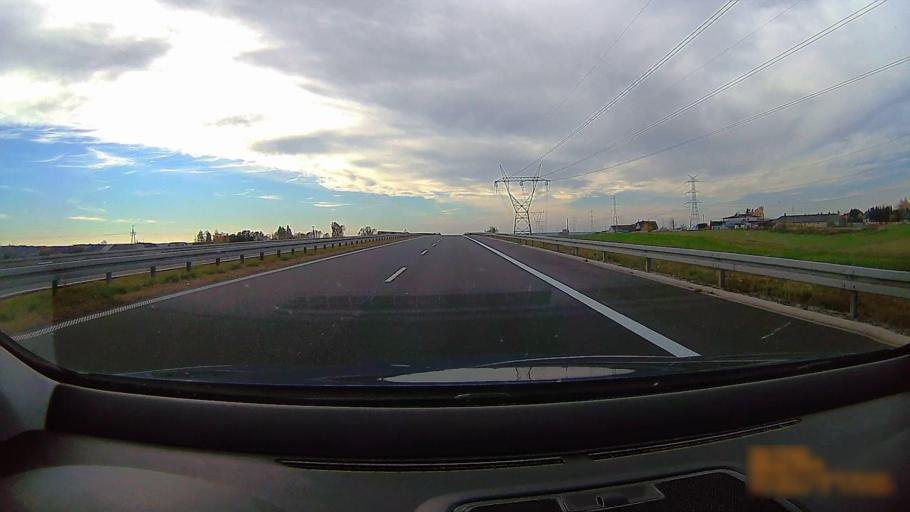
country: PL
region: Greater Poland Voivodeship
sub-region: Powiat ostrowski
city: Przygodzice
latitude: 51.6074
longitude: 17.8553
